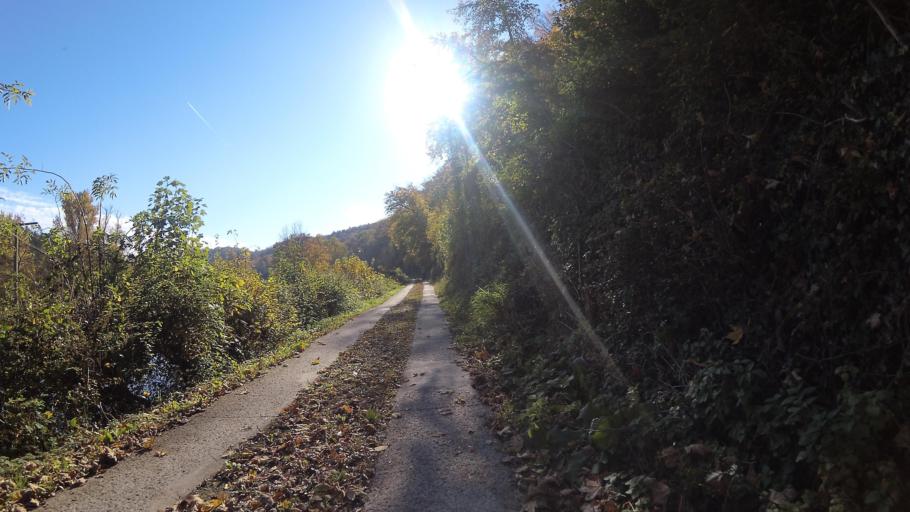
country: DE
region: Baden-Wuerttemberg
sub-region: Regierungsbezirk Stuttgart
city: Jagsthausen
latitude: 49.2748
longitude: 9.4469
